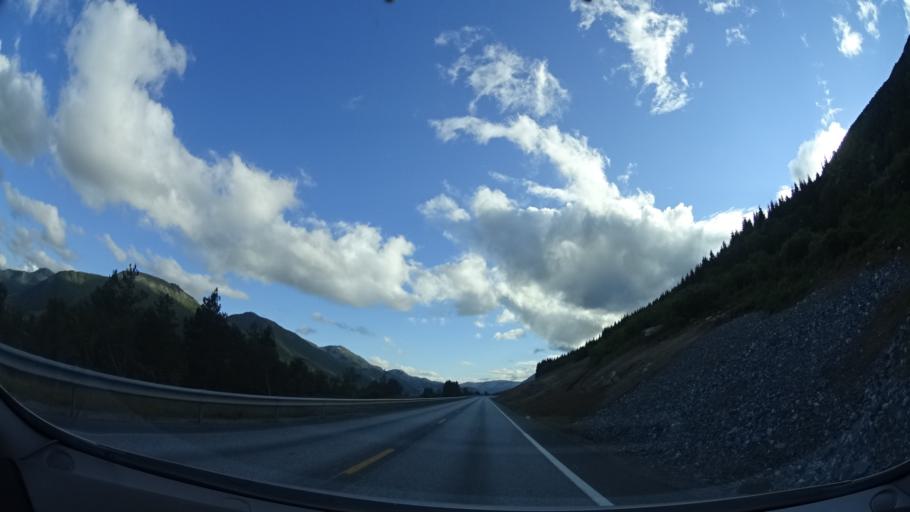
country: NO
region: More og Romsdal
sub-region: Gjemnes
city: Batnfjordsora
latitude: 62.9345
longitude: 7.7295
